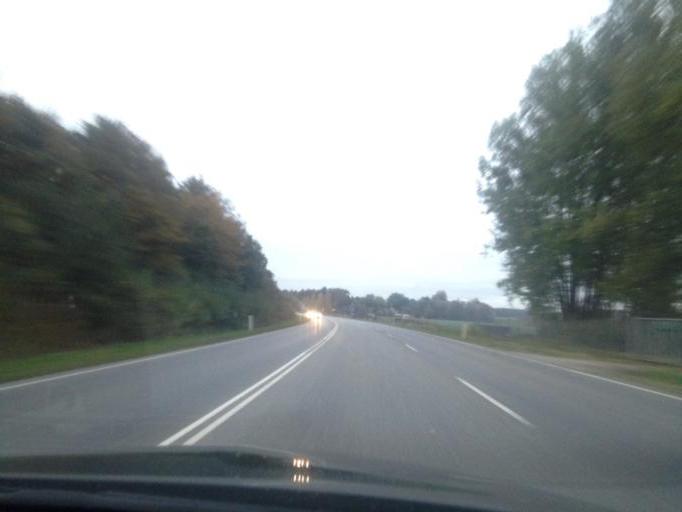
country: DK
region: Zealand
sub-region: Roskilde Kommune
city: Roskilde
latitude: 55.6081
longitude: 12.1014
